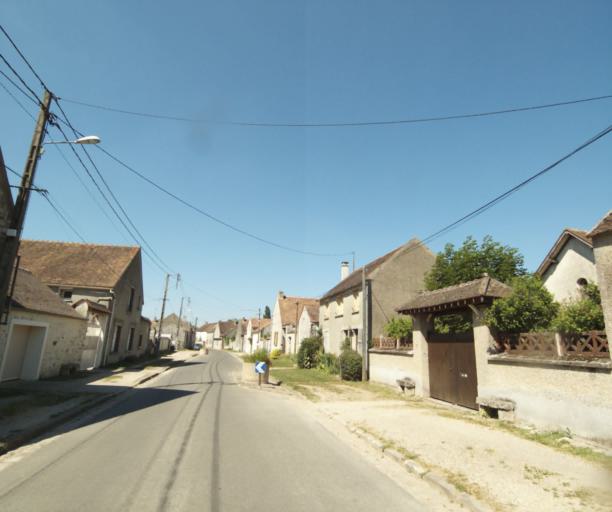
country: FR
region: Ile-de-France
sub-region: Departement de Seine-et-Marne
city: Acheres-la-Foret
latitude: 48.3434
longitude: 2.5646
